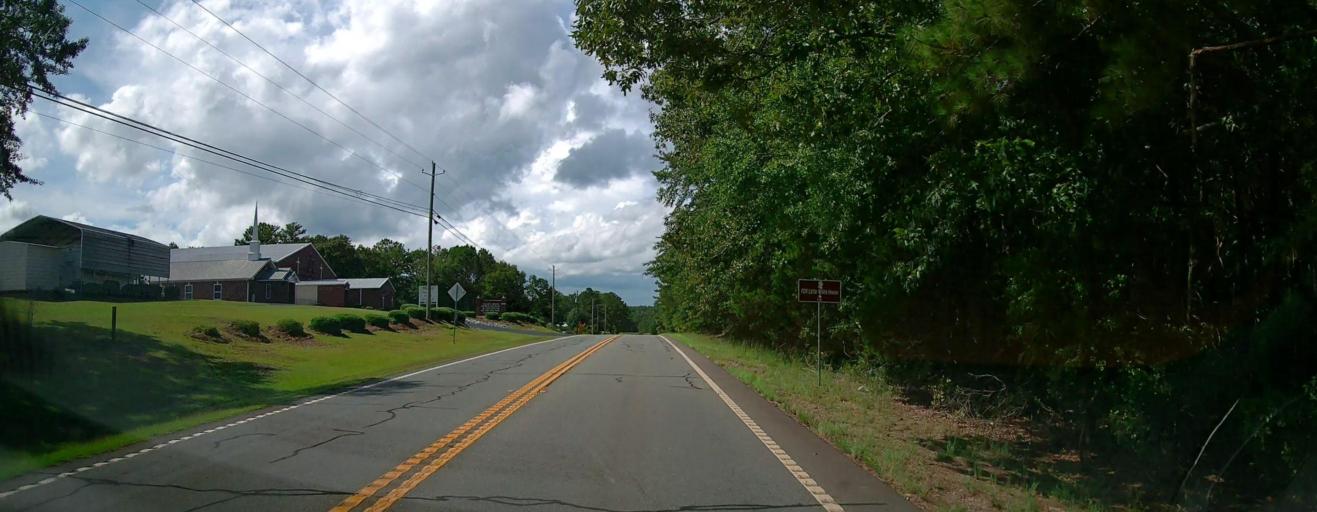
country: US
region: Georgia
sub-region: Talbot County
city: Sardis
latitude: 32.8124
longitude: -84.5989
